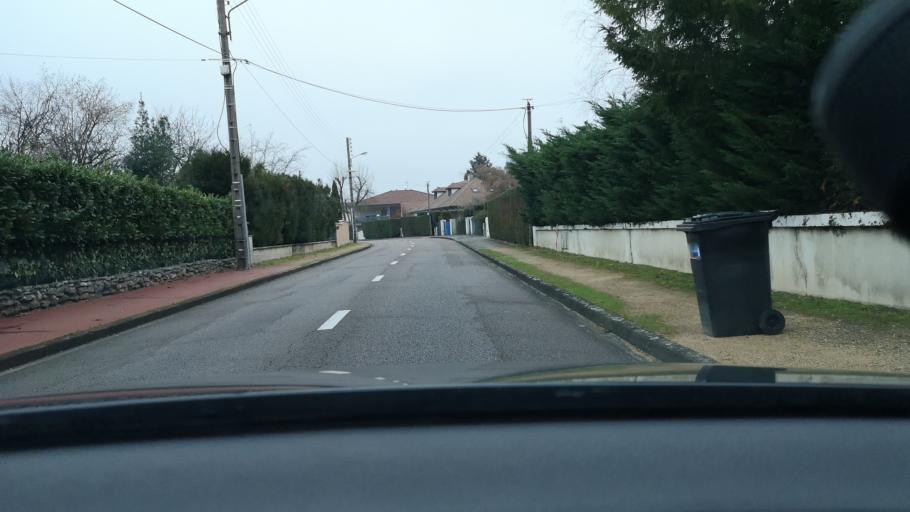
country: FR
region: Bourgogne
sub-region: Departement de Saone-et-Loire
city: Chalon-sur-Saone
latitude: 46.8037
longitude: 4.8494
